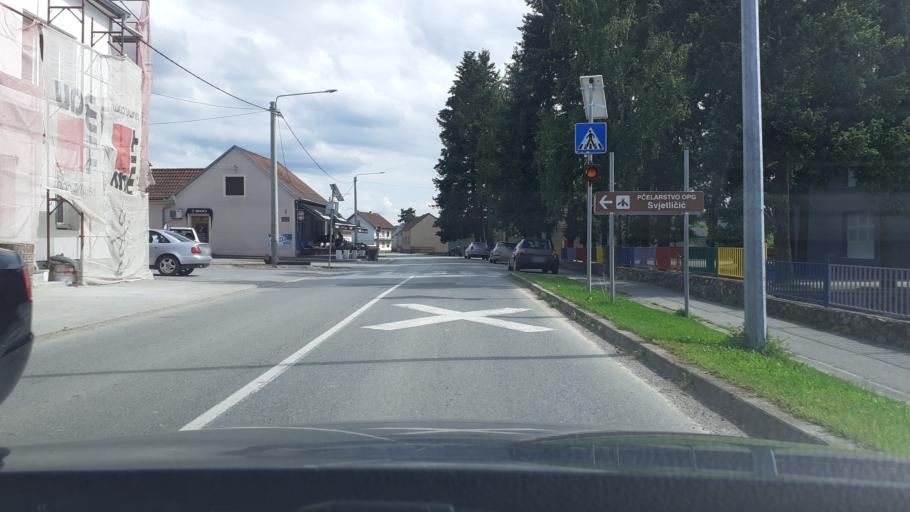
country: HR
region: Pozesko-Slavonska
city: Jaksic
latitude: 45.3561
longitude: 17.7621
